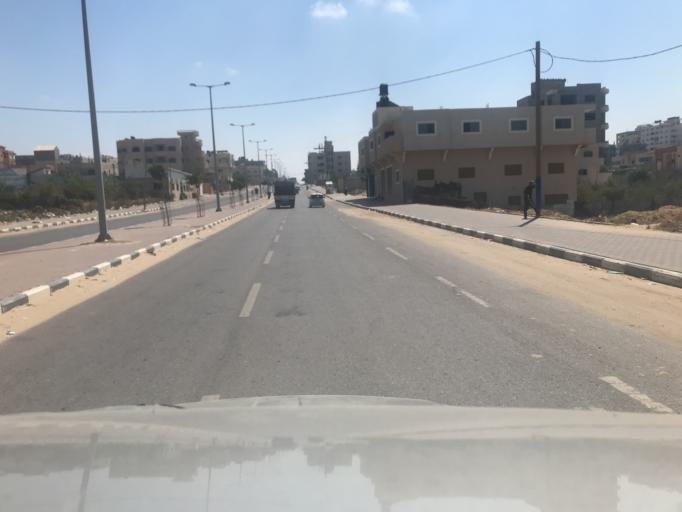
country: PS
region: Gaza Strip
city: Bayt Lahya
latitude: 31.5517
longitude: 34.4703
